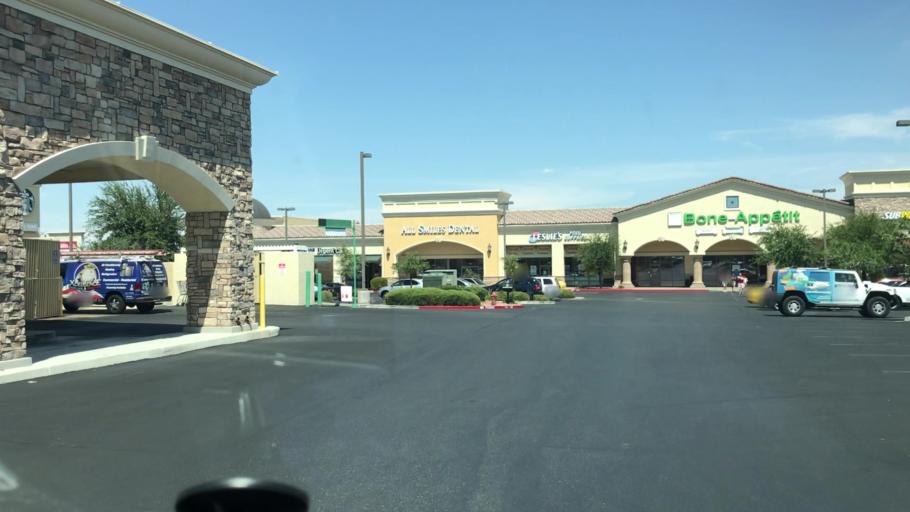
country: US
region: Nevada
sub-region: Clark County
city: Enterprise
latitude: 35.9977
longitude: -115.2067
